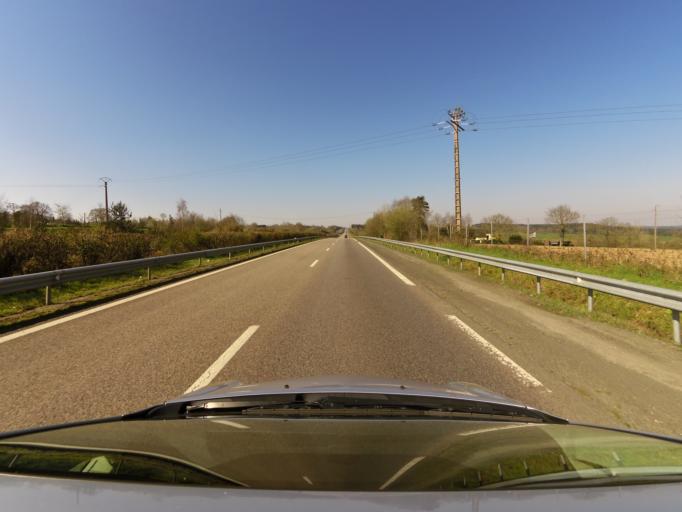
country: FR
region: Brittany
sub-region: Departement d'Ille-et-Vilaine
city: Saint-Thurial
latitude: 48.0396
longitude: -1.9605
